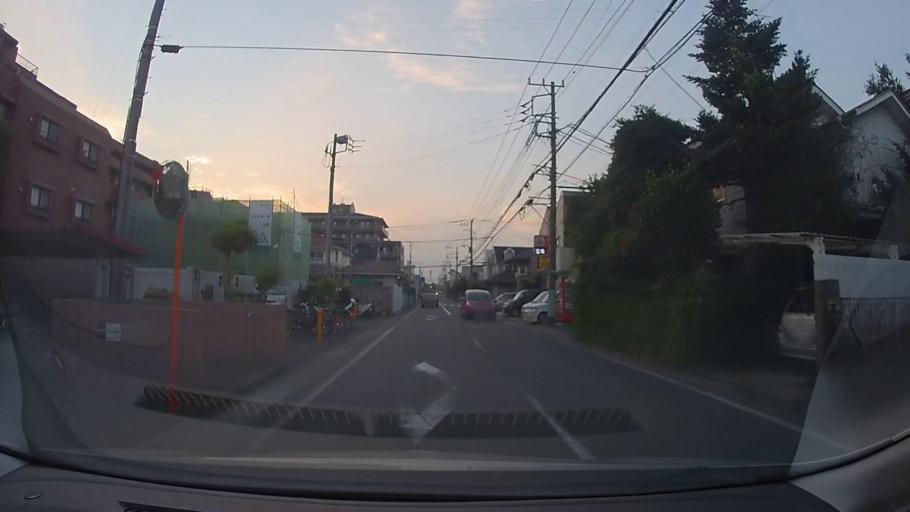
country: JP
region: Kanagawa
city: Minami-rinkan
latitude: 35.4955
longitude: 139.4437
